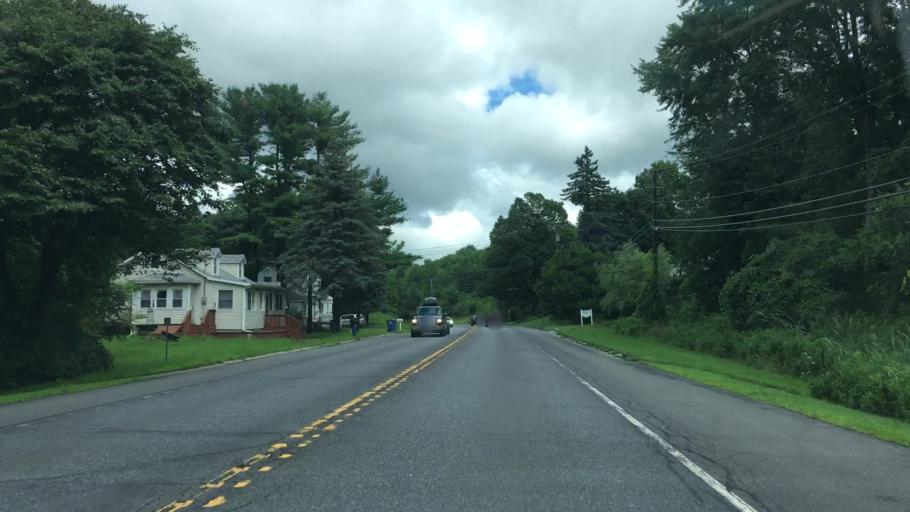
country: US
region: New York
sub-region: Rensselaer County
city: Poestenkill
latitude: 42.7896
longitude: -73.5717
